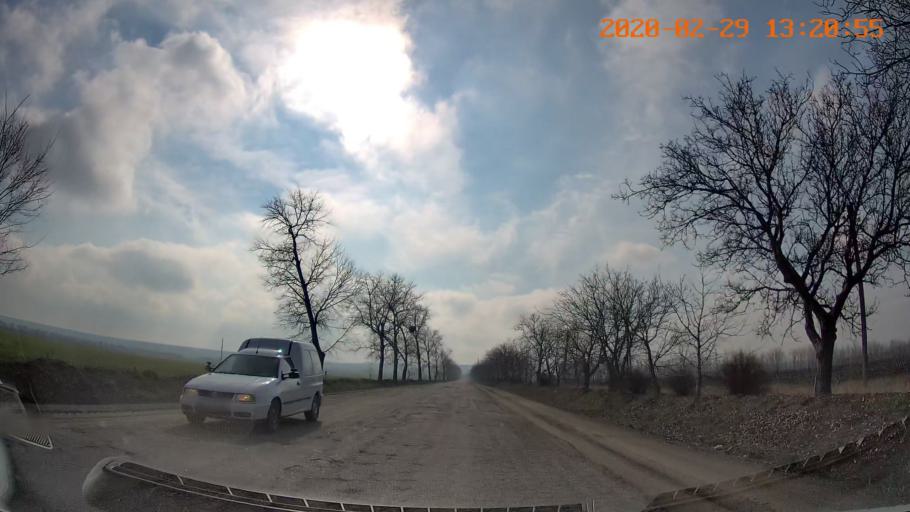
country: MD
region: Telenesti
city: Camenca
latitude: 47.9747
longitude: 28.6373
